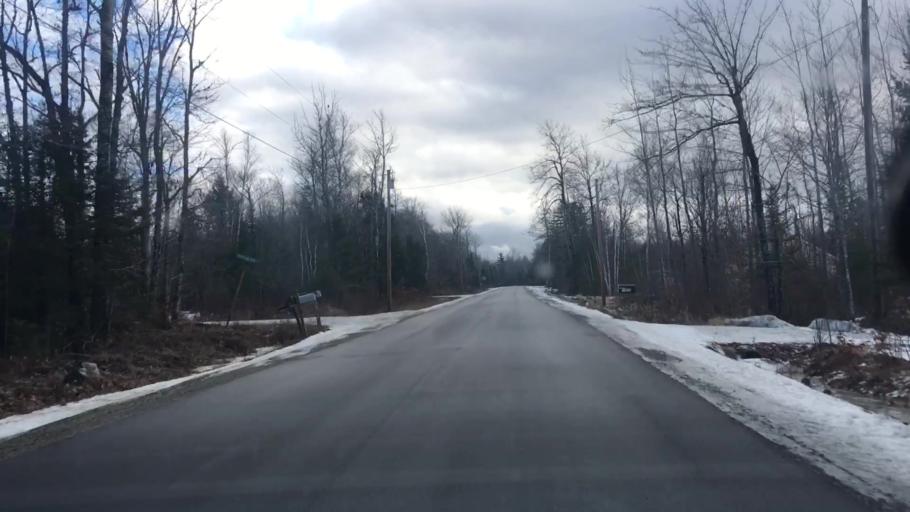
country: US
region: Maine
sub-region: Hancock County
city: Dedham
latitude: 44.6829
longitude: -68.7085
